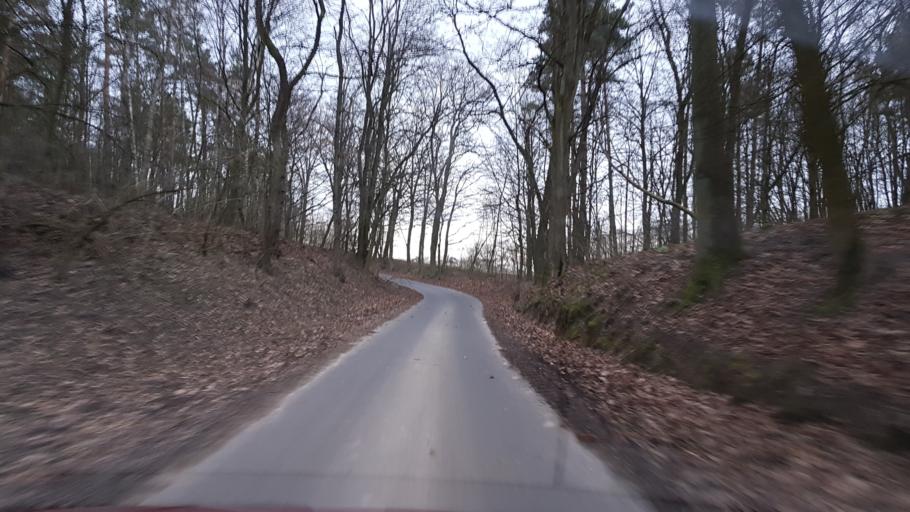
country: PL
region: West Pomeranian Voivodeship
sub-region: Powiat mysliborski
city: Barlinek
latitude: 53.0486
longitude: 15.2235
